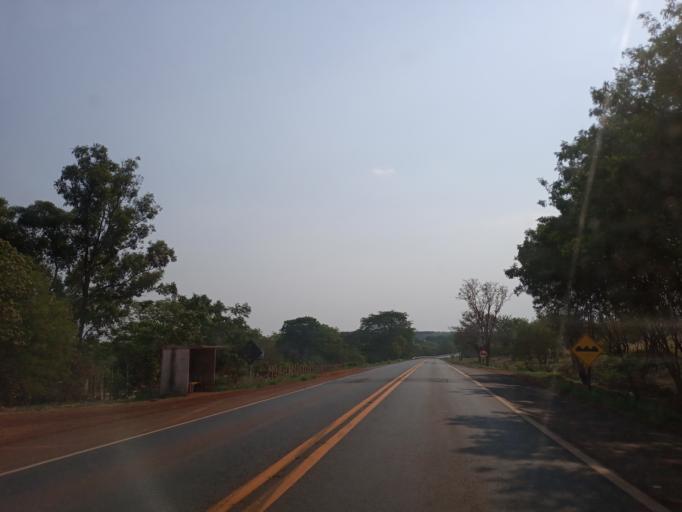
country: BR
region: Minas Gerais
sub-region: Ituiutaba
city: Ituiutaba
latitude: -18.9647
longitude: -49.4813
